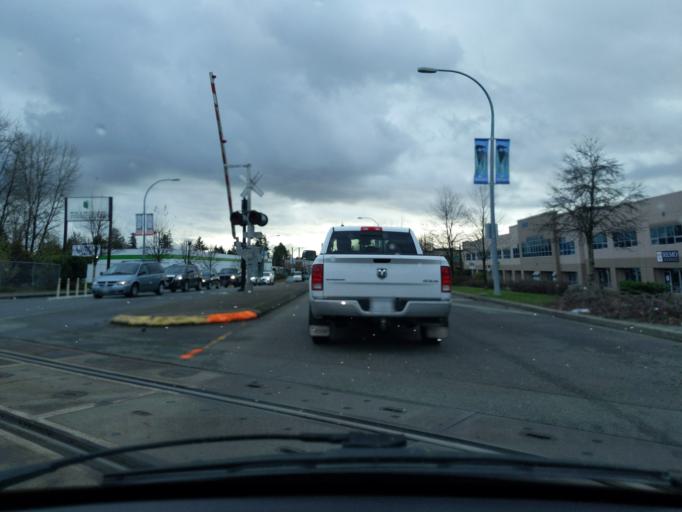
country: CA
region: British Columbia
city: Pitt Meadows
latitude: 49.2120
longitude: -122.6588
